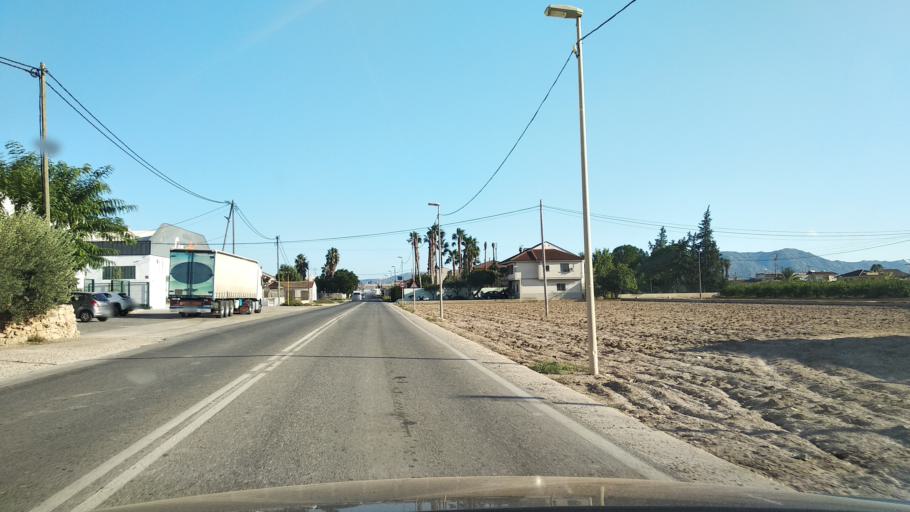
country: ES
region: Murcia
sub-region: Murcia
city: Santomera
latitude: 38.0420
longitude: -1.0499
